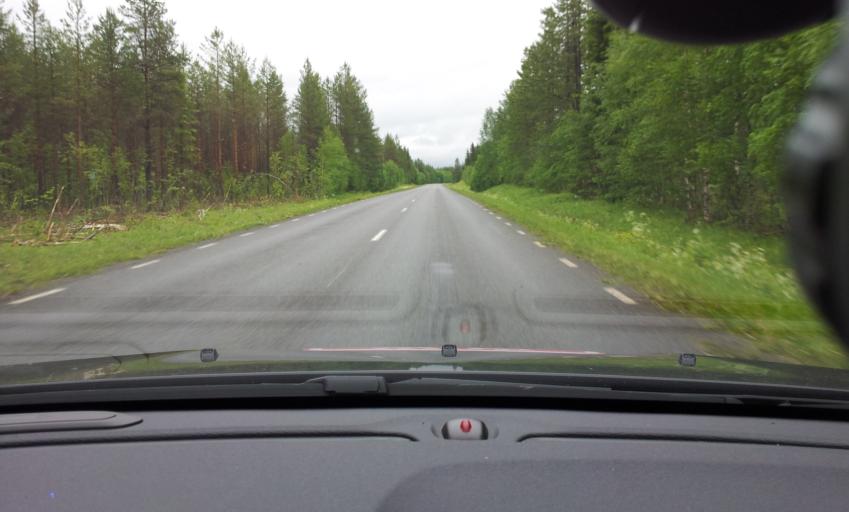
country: SE
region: Jaemtland
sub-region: Stroemsunds Kommun
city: Stroemsund
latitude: 63.6042
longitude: 15.2977
